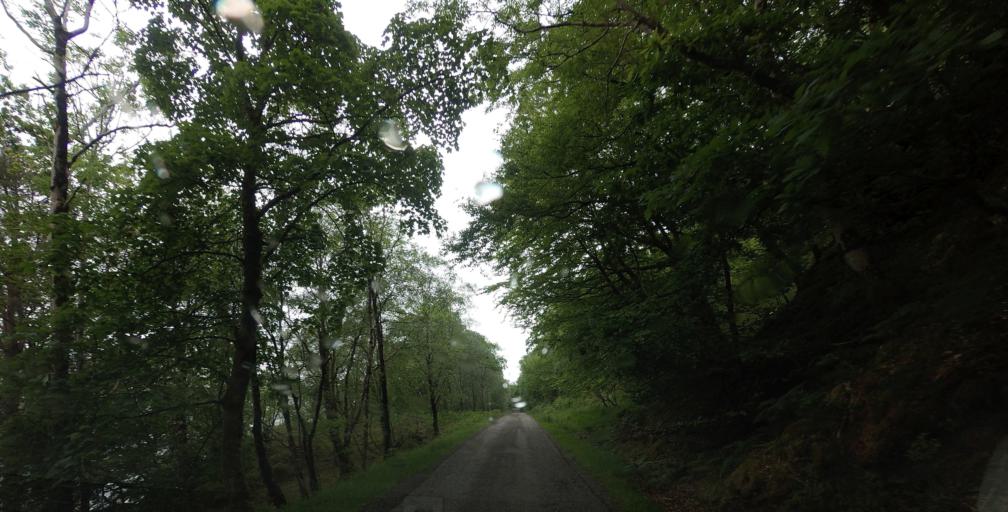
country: GB
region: Scotland
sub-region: Highland
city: Fort William
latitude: 56.7933
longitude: -5.1716
